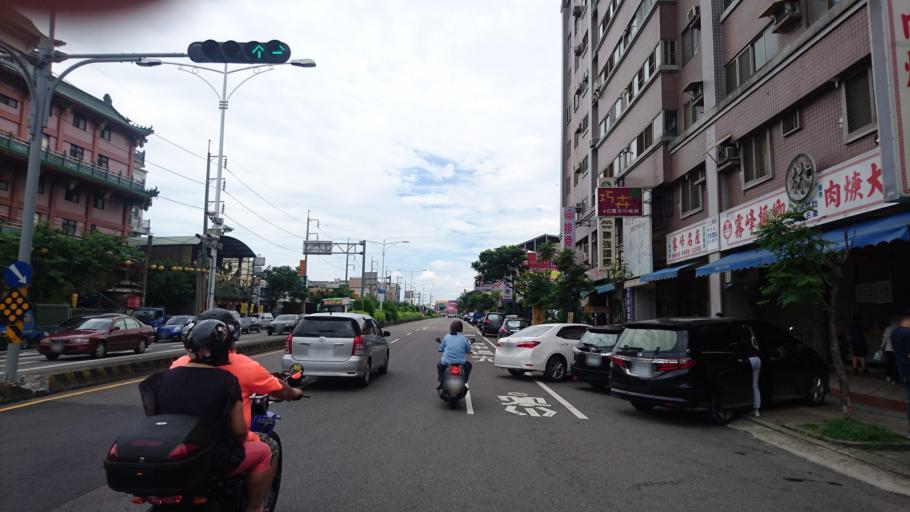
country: TW
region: Taiwan
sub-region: Taichung City
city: Taichung
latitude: 24.0658
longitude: 120.6961
